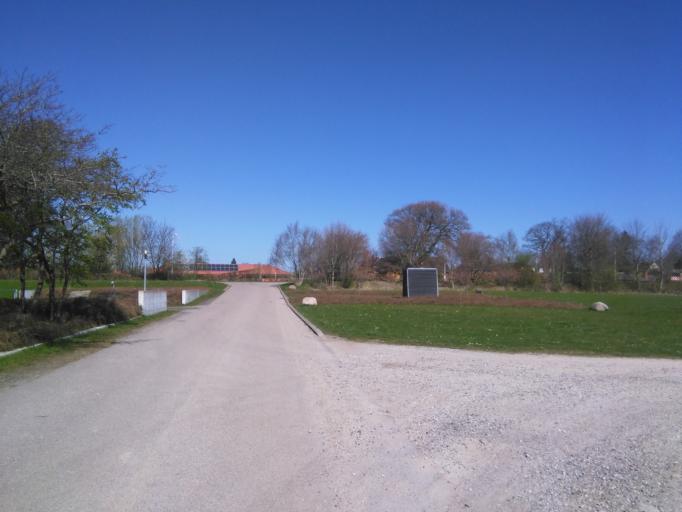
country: DK
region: Central Jutland
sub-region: Arhus Kommune
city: Tranbjerg
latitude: 56.0830
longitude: 10.1380
